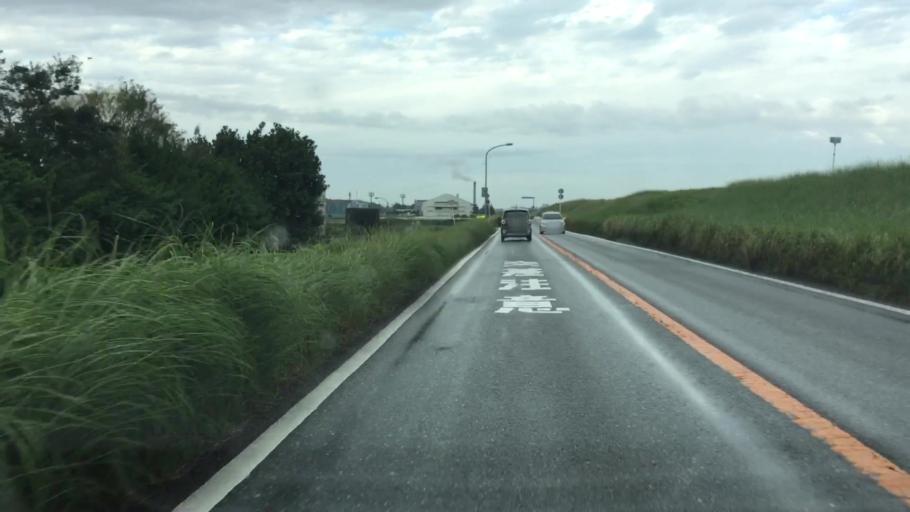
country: JP
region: Ibaraki
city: Toride
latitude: 35.8736
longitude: 140.1097
